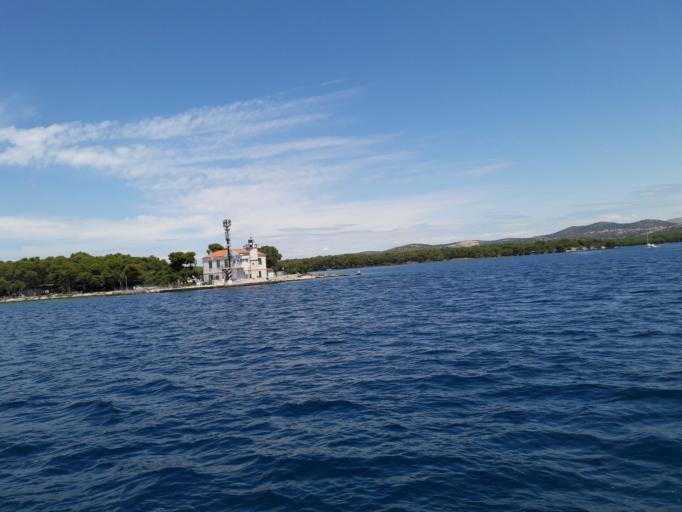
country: HR
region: Sibensko-Kniniska
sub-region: Grad Sibenik
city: Sibenik
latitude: 43.7204
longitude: 15.8499
